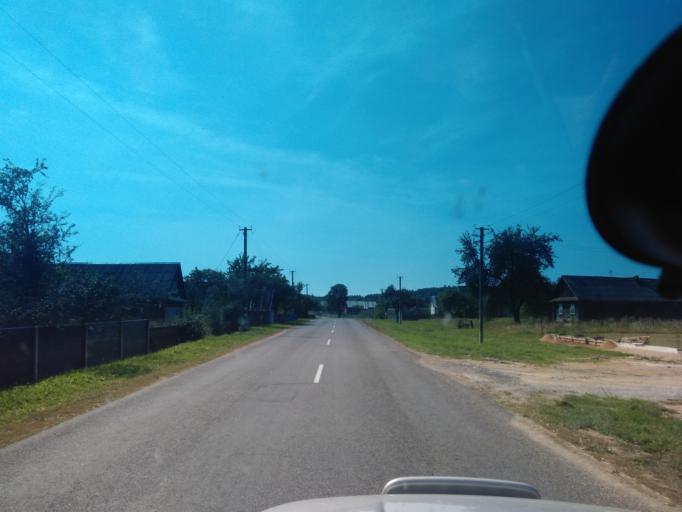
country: BY
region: Minsk
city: Kapyl'
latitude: 53.2037
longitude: 27.1186
